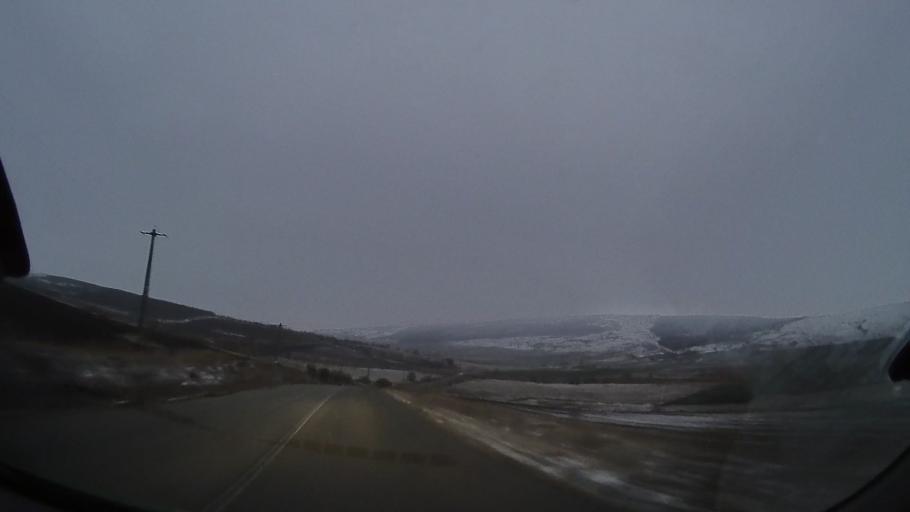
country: RO
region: Vaslui
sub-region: Comuna Vutcani
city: Vutcani
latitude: 46.4028
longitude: 27.9867
